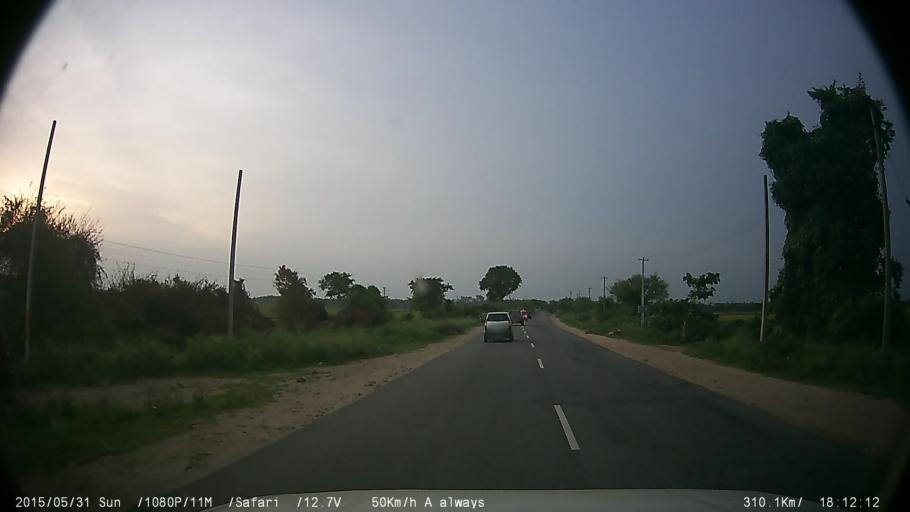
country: IN
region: Karnataka
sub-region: Mysore
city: Nanjangud
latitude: 12.0940
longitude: 76.6726
